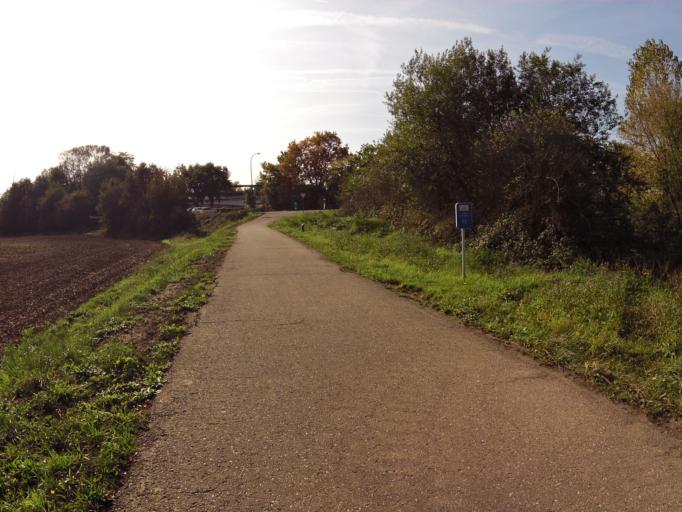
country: BE
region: Flanders
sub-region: Provincie Limburg
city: Maasmechelen
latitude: 50.9609
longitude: 5.7102
